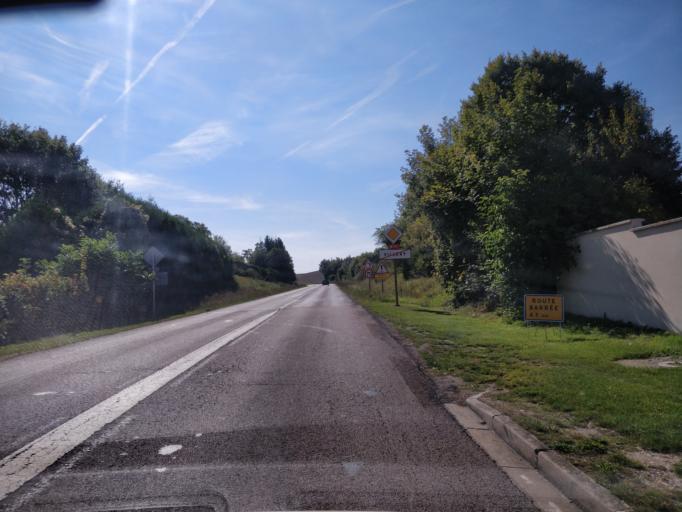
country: FR
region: Champagne-Ardenne
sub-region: Departement de l'Aube
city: Bouilly
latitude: 48.1682
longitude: 4.0212
